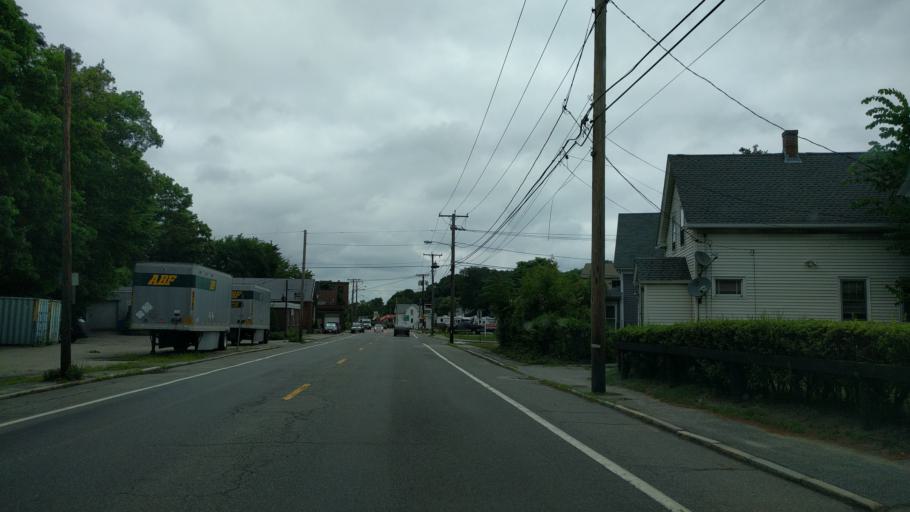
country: US
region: Massachusetts
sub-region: Worcester County
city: Worcester
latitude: 42.2292
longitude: -71.8203
